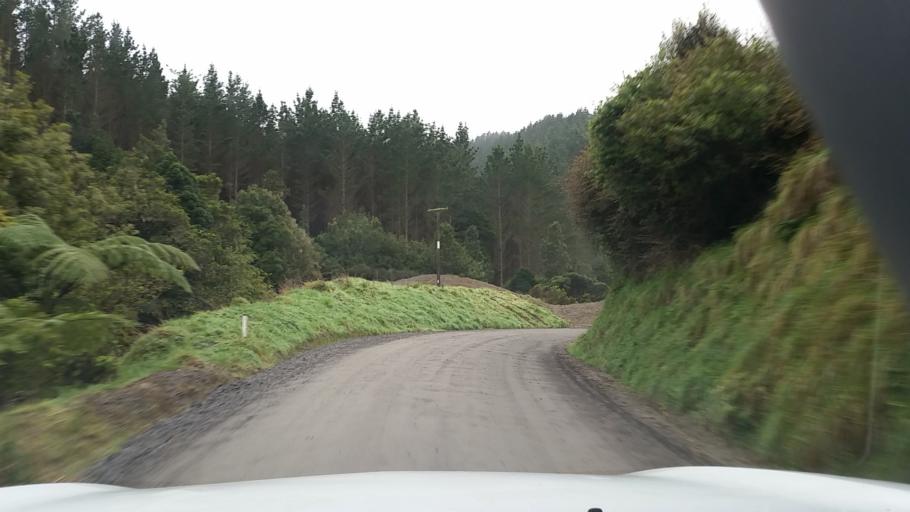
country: NZ
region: Taranaki
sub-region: South Taranaki District
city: Eltham
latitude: -39.5221
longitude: 174.4158
